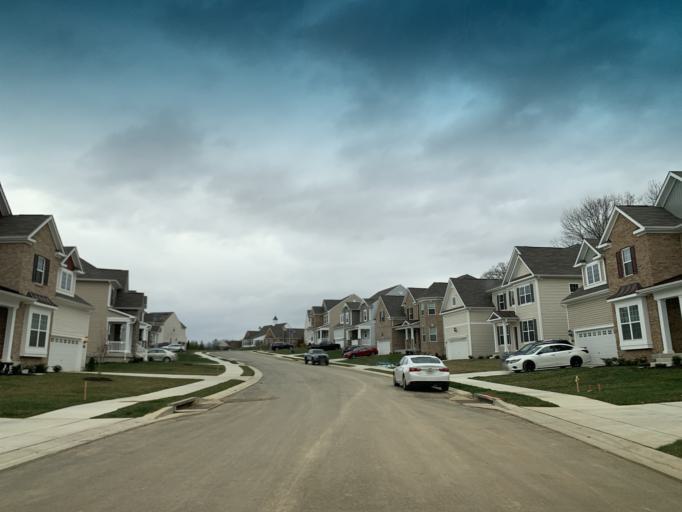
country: US
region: Maryland
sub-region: Harford County
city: Perryman
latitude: 39.5006
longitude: -76.2047
